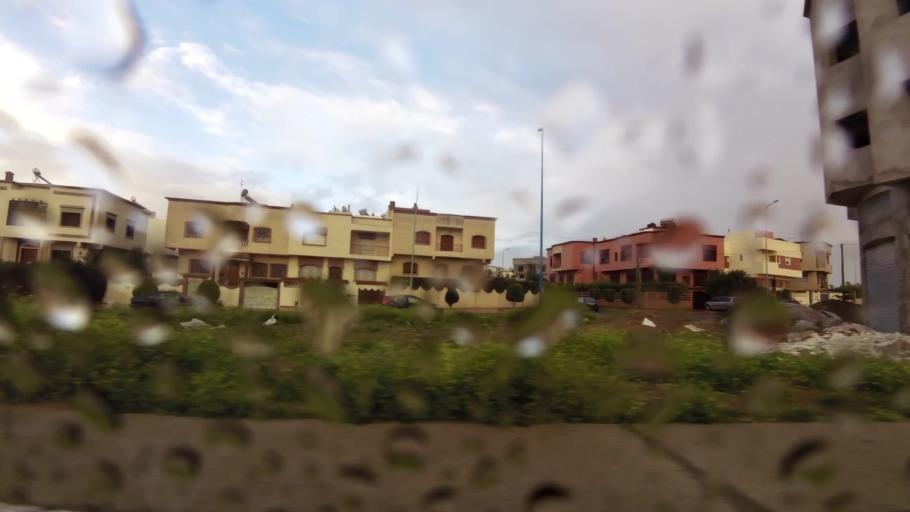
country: MA
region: Doukkala-Abda
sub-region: El-Jadida
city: El Jadida
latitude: 33.2416
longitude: -8.5150
